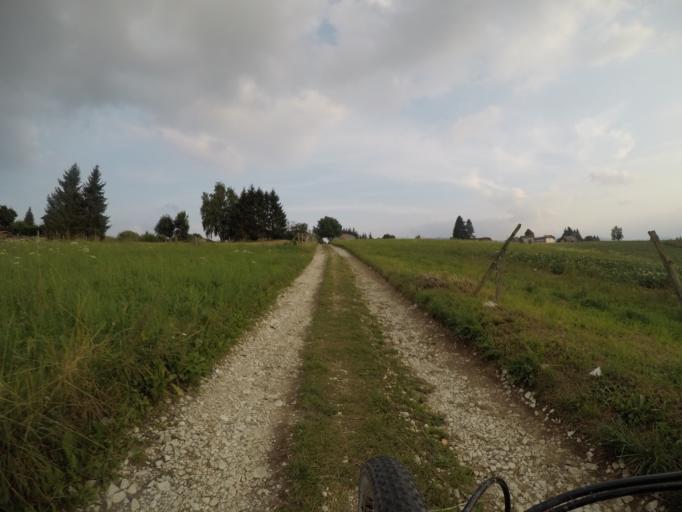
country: IT
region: Veneto
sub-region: Provincia di Vicenza
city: Gallio
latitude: 45.8736
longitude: 11.5334
